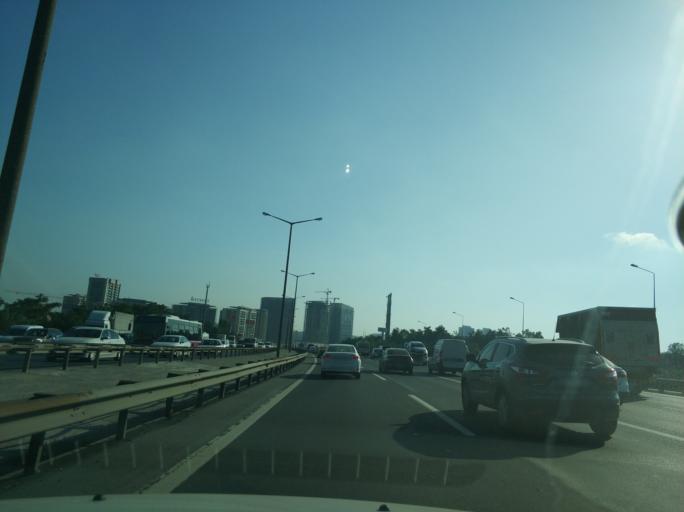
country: TR
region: Istanbul
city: Sisli
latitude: 41.0970
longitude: 28.9529
